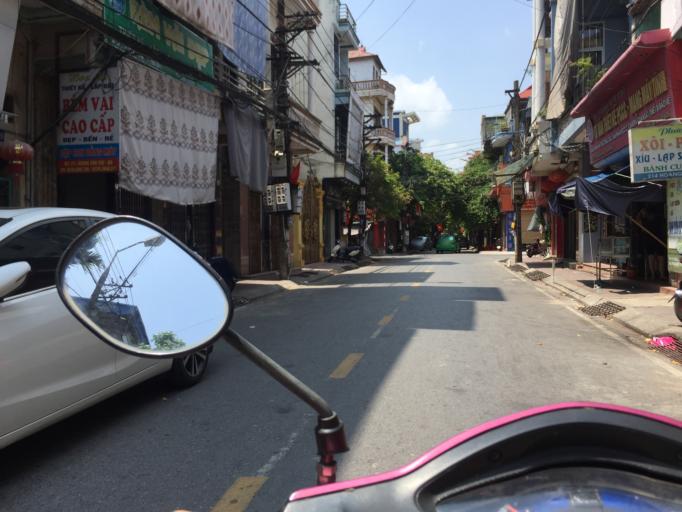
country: VN
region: Nam Dinh
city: Thanh Pho Nam Dinh
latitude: 20.4275
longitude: 106.1764
